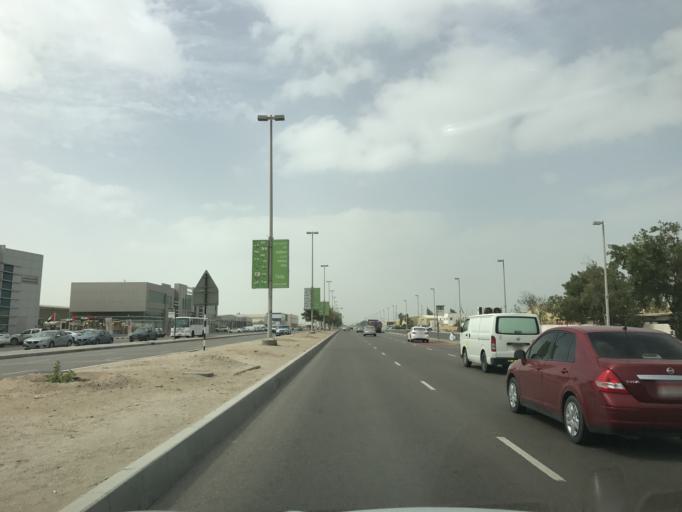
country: AE
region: Abu Dhabi
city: Abu Dhabi
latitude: 24.3819
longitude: 54.4981
